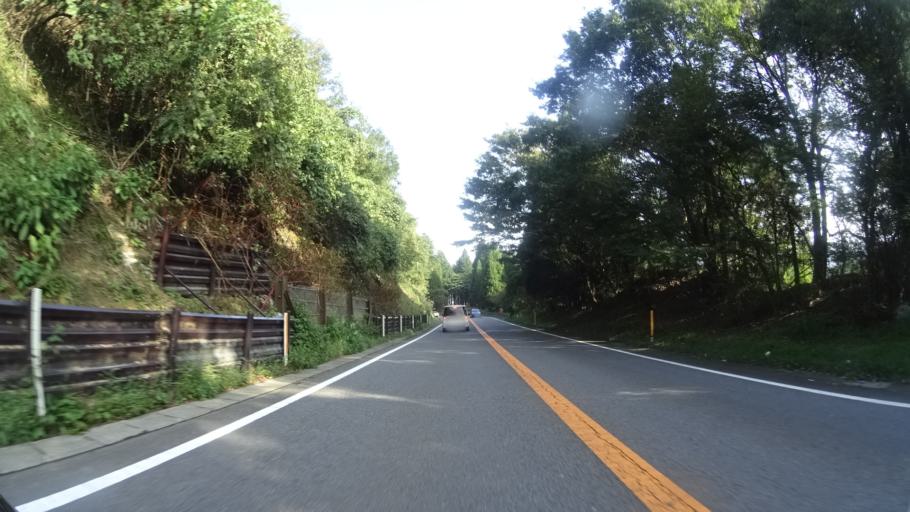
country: JP
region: Oita
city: Tsukawaki
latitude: 33.2530
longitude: 131.3028
